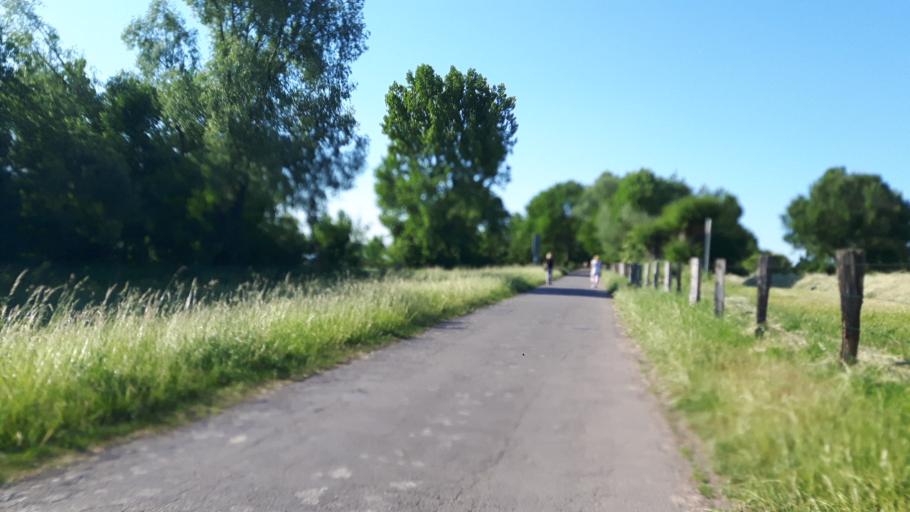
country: DE
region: North Rhine-Westphalia
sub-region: Regierungsbezirk Dusseldorf
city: Meerbusch
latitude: 51.3129
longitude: 6.7376
